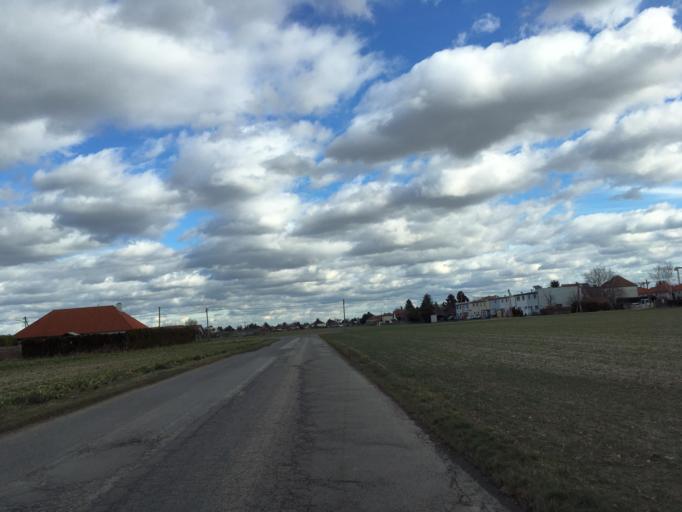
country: AT
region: Lower Austria
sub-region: Politischer Bezirk Ganserndorf
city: Gross-Enzersdorf
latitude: 48.2111
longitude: 16.5019
